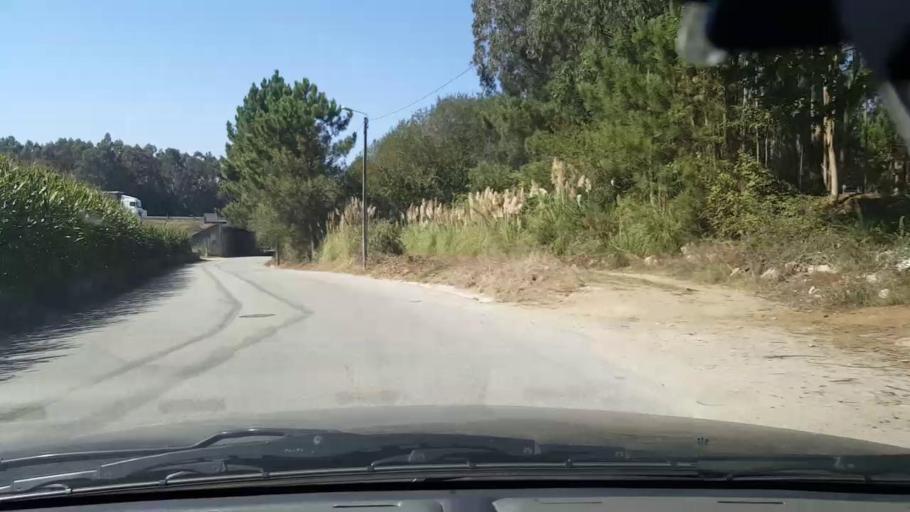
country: PT
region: Porto
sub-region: Matosinhos
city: Lavra
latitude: 41.2760
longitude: -8.6985
